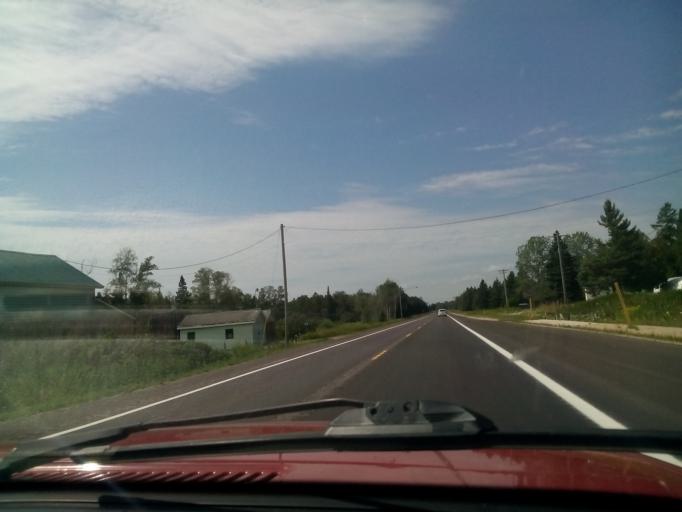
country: US
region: Michigan
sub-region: Schoolcraft County
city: Manistique
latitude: 45.9920
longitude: -86.0187
